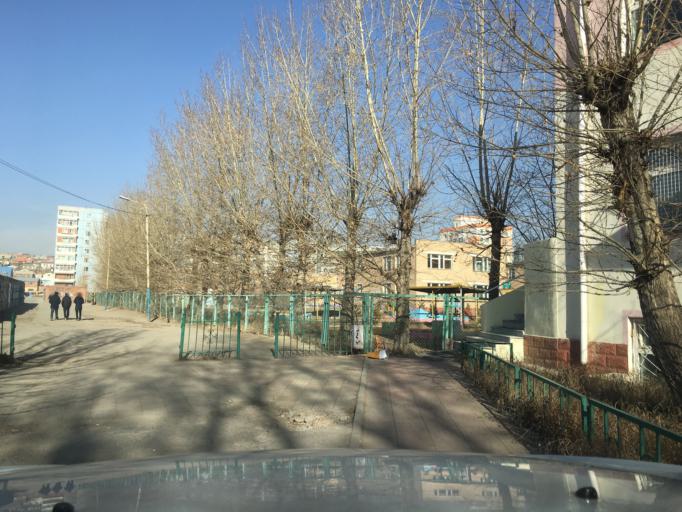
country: MN
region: Ulaanbaatar
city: Ulaanbaatar
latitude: 47.9141
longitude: 106.8431
